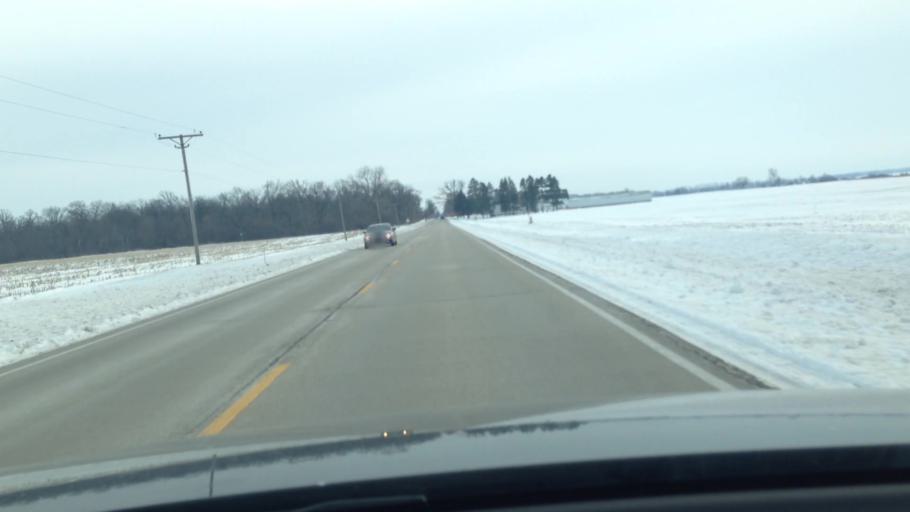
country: US
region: Illinois
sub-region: McHenry County
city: Hebron
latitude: 42.4249
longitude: -88.4381
